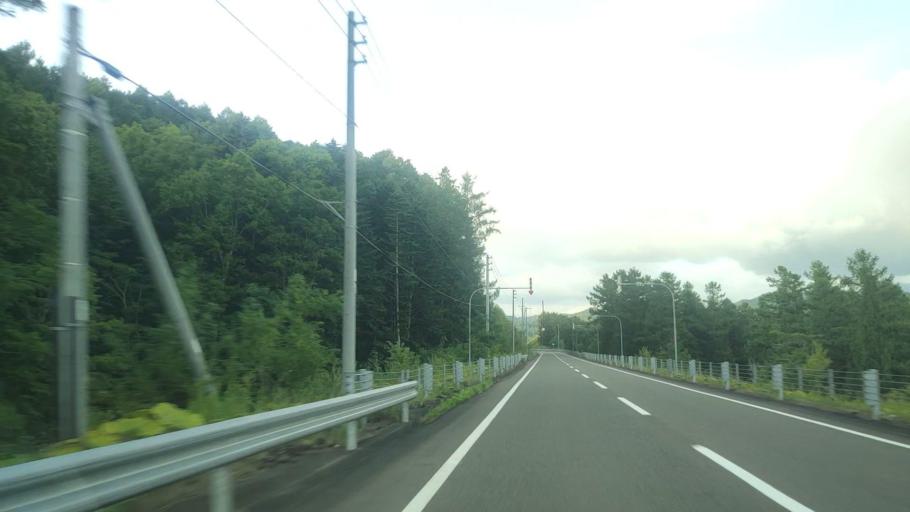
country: JP
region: Hokkaido
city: Bibai
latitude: 43.0661
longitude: 142.1018
